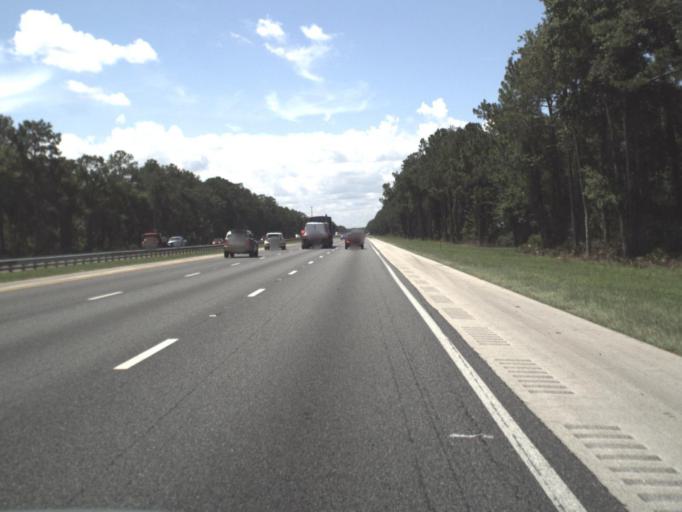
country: US
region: Florida
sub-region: Saint Johns County
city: Saint Augustine
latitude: 29.8778
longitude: -81.4002
